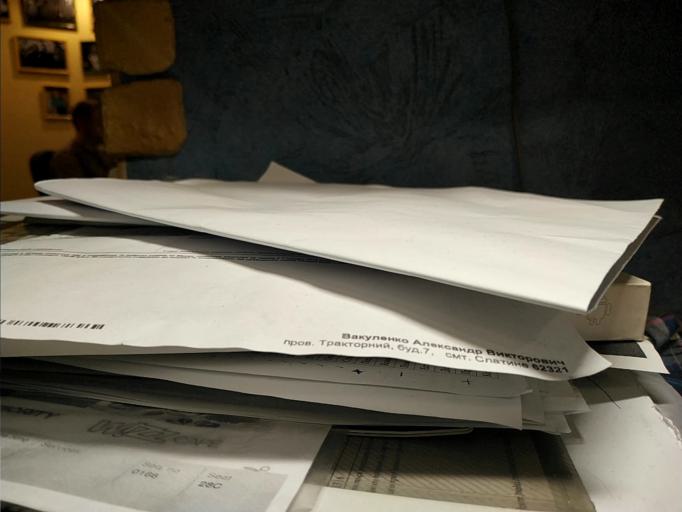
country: RU
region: Tverskaya
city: Zubtsov
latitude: 56.1183
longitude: 34.5842
